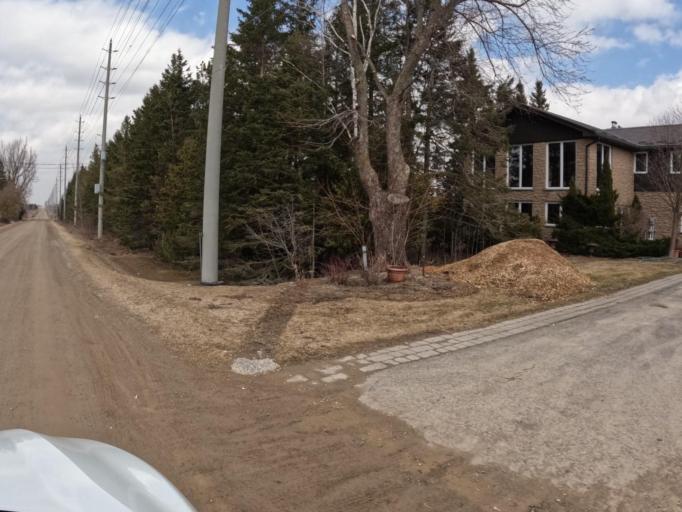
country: CA
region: Ontario
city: Shelburne
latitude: 44.0189
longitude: -80.3125
